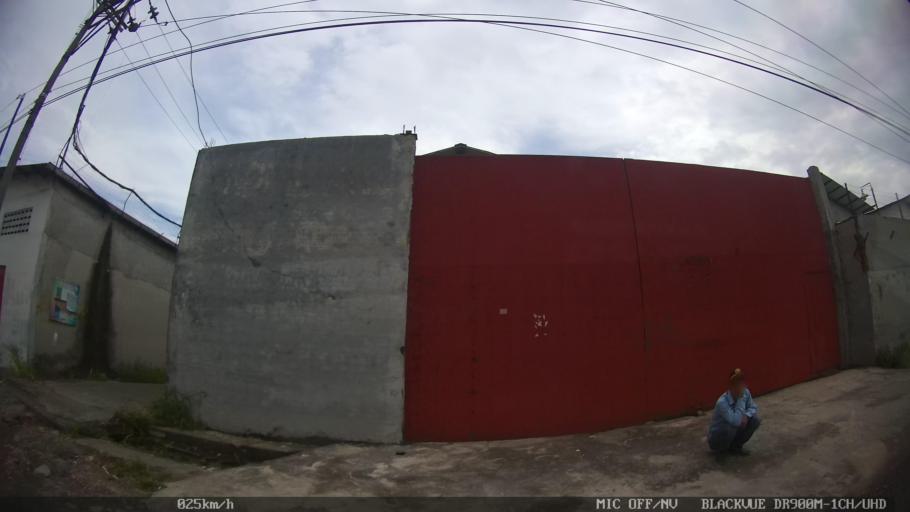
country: ID
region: North Sumatra
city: Sunggal
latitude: 3.6146
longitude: 98.5852
